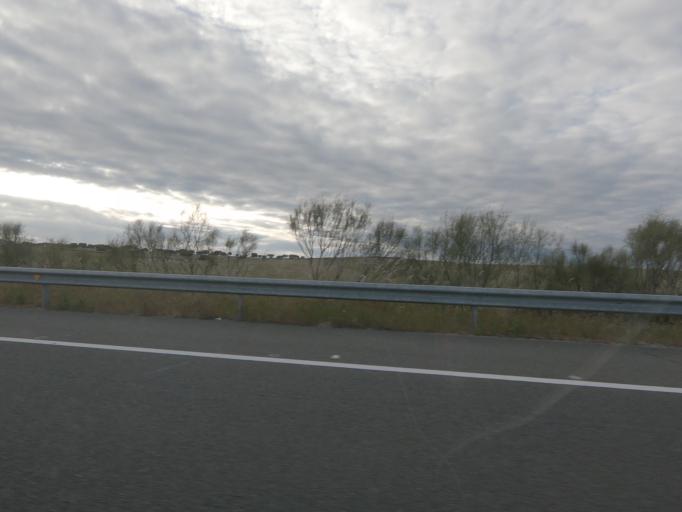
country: ES
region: Extremadura
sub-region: Provincia de Caceres
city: Casar de Caceres
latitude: 39.5343
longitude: -6.4114
